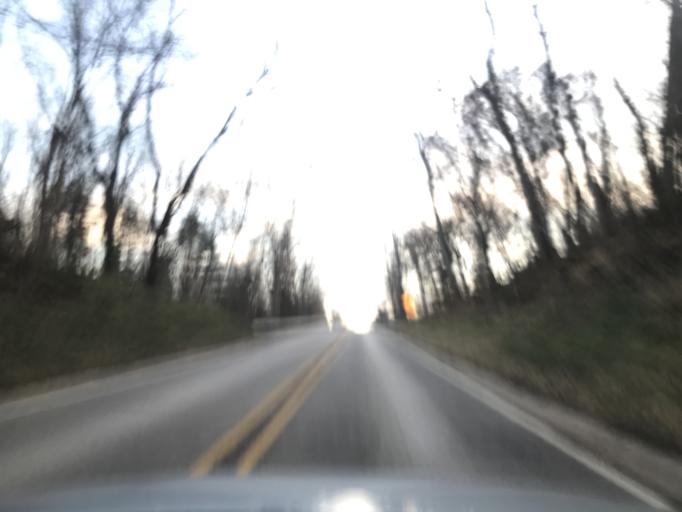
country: US
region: Illinois
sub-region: Henderson County
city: Oquawka
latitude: 40.9007
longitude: -90.8645
